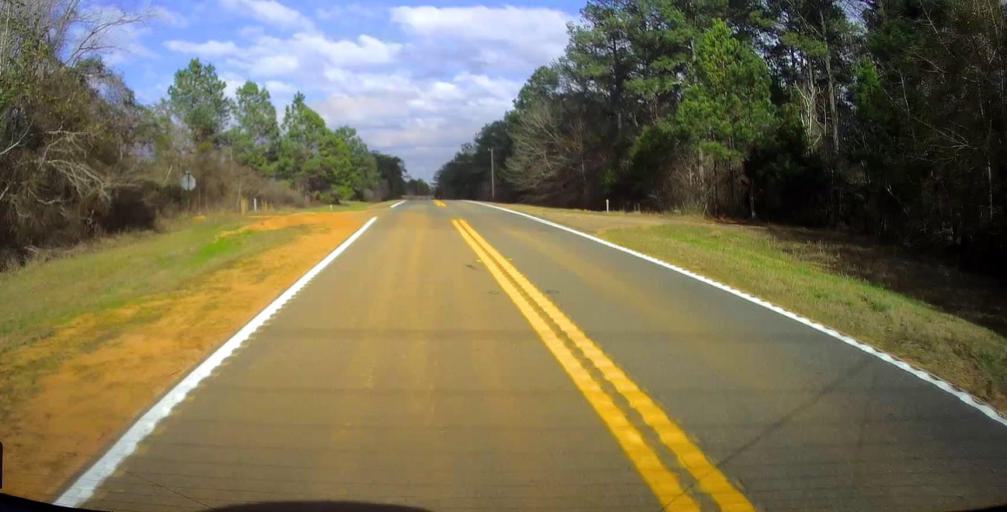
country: US
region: Georgia
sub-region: Marion County
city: Buena Vista
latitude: 32.4433
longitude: -84.4751
